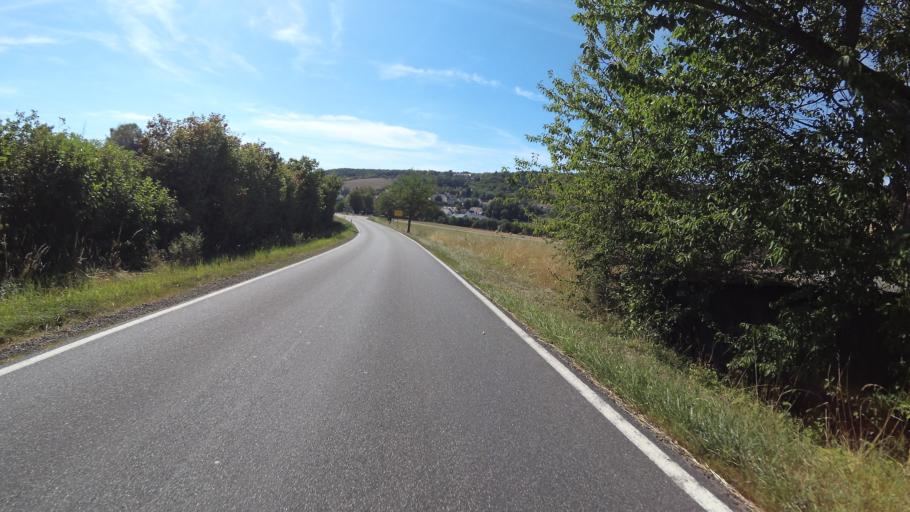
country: DE
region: Saarland
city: Gersheim
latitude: 49.1553
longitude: 7.2413
